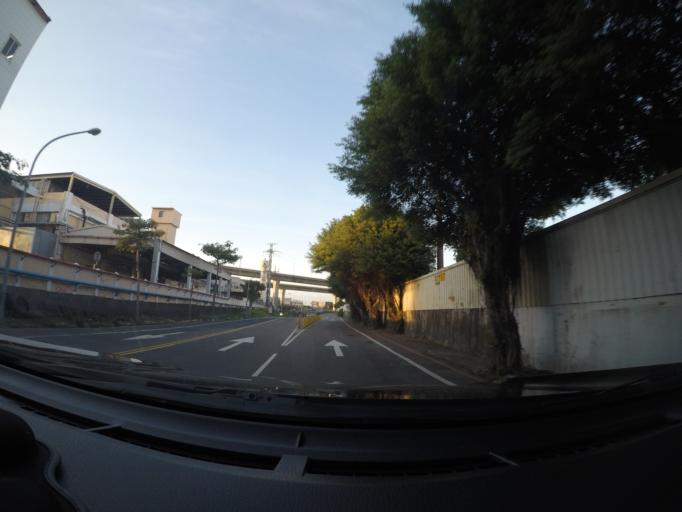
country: TW
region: Taiwan
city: Taoyuan City
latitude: 24.9938
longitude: 121.2454
